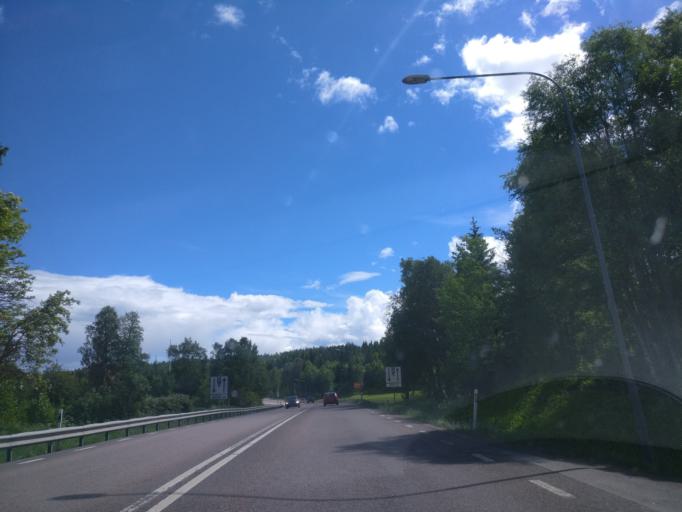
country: SE
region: Vaesternorrland
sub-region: Haernoesands Kommun
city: Haernoesand
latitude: 62.6607
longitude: 17.8589
